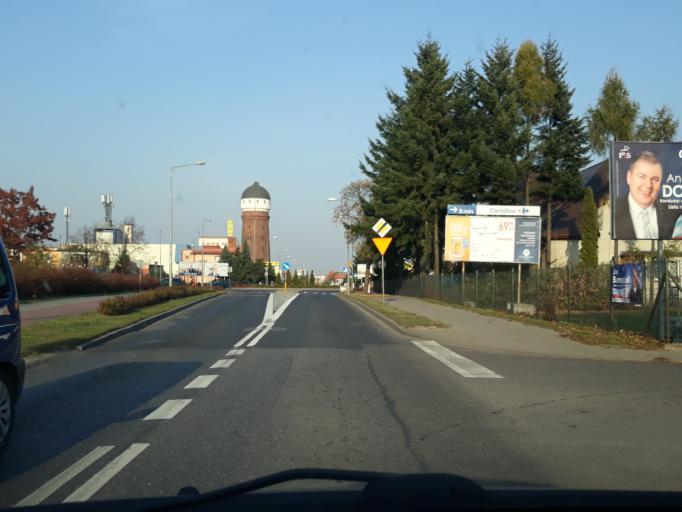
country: PL
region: Pomeranian Voivodeship
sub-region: Powiat chojnicki
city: Chojnice
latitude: 53.6892
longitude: 17.5508
